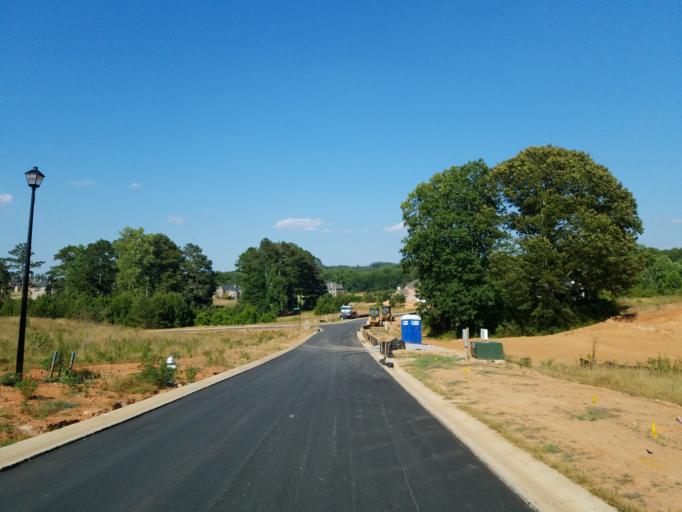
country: US
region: Georgia
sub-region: Fulton County
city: Milton
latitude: 34.1796
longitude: -84.3303
